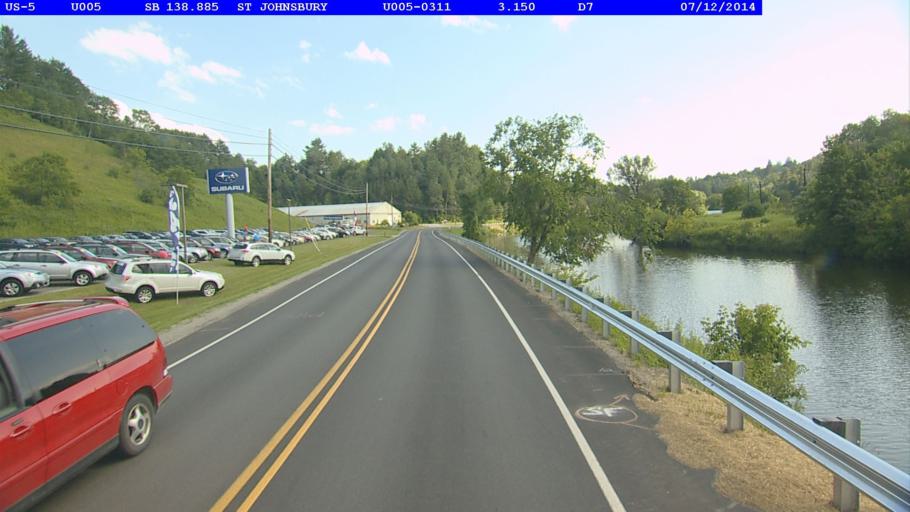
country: US
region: Vermont
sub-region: Caledonia County
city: St Johnsbury
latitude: 44.4374
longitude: -72.0163
